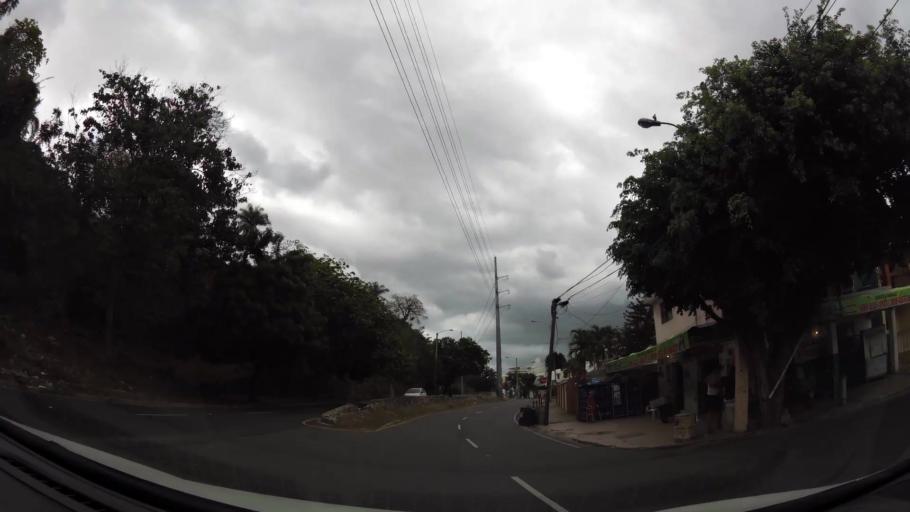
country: DO
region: Nacional
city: Bella Vista
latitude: 18.4444
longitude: -69.9460
